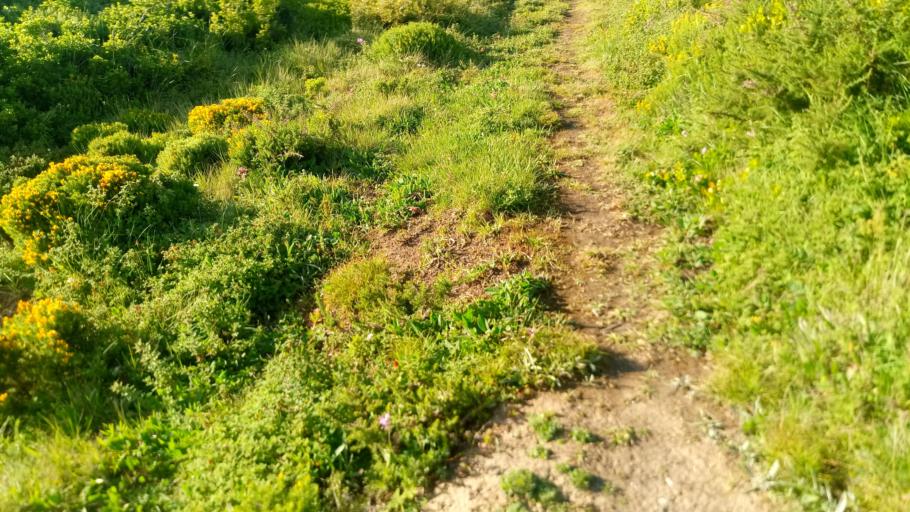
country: PT
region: Leiria
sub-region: Caldas da Rainha
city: Caldas da Rainha
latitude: 39.4607
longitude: -9.1957
